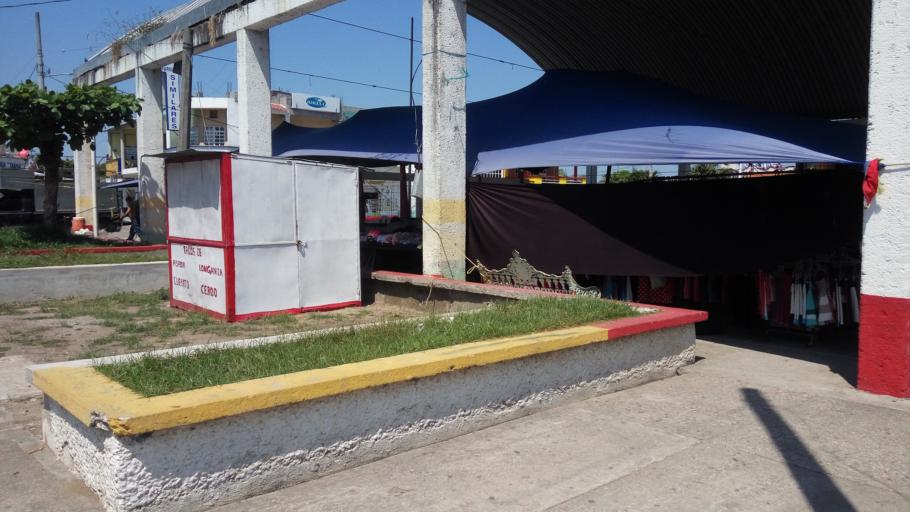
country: MX
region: Tabasco
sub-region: Centla
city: Ignacio Zaragoza
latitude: 18.4018
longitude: -92.9559
